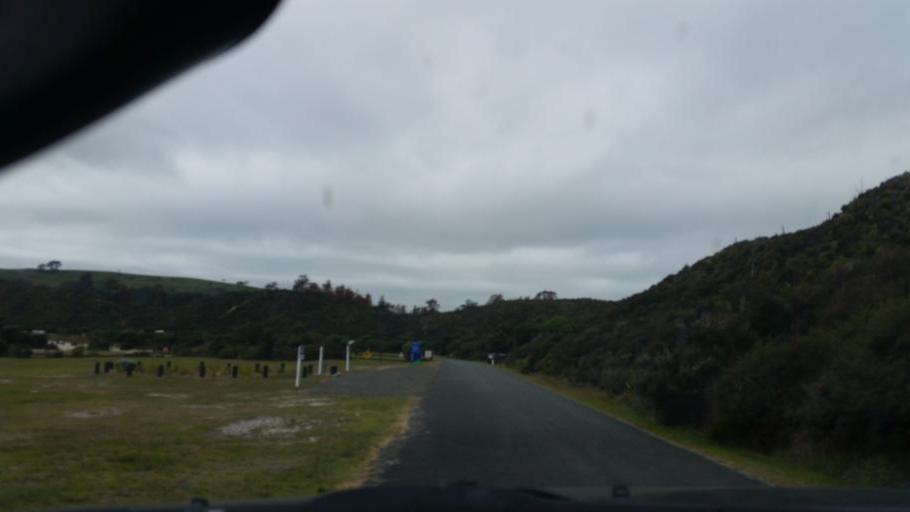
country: NZ
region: Northland
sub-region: Kaipara District
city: Dargaville
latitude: -35.8116
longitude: 173.6612
